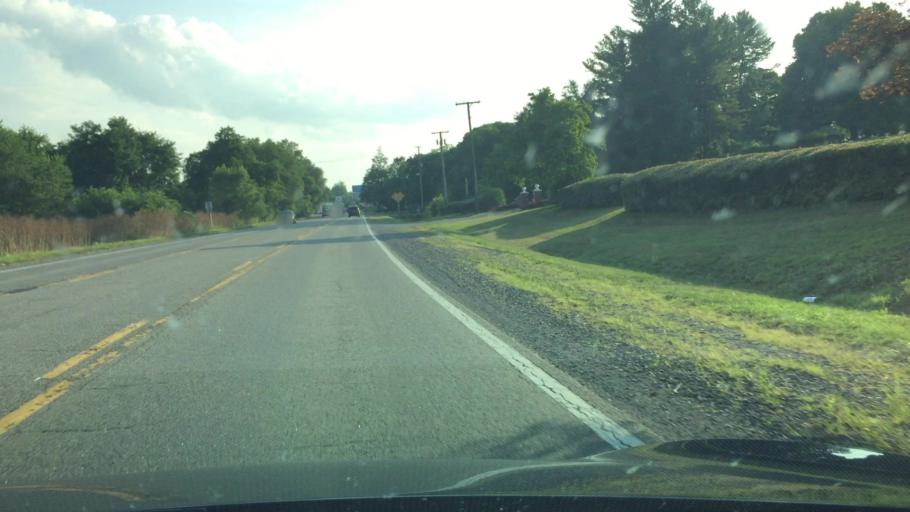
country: US
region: Virginia
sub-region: Pulaski County
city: Dublin
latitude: 37.1124
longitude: -80.6739
